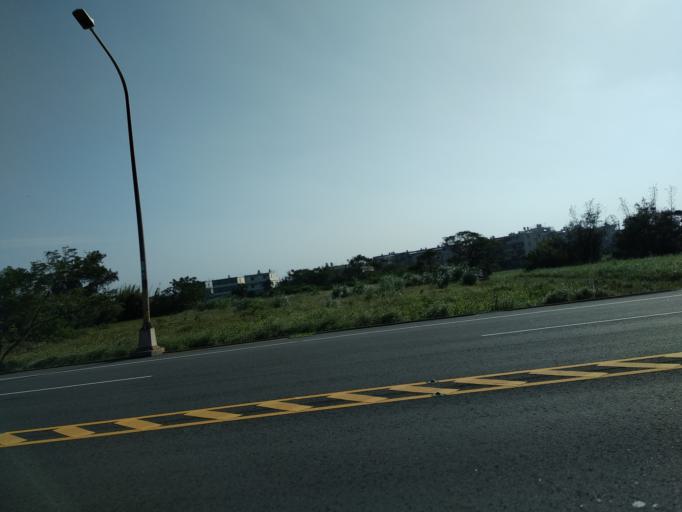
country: TW
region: Taiwan
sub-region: Hsinchu
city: Zhubei
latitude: 24.9844
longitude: 121.0552
